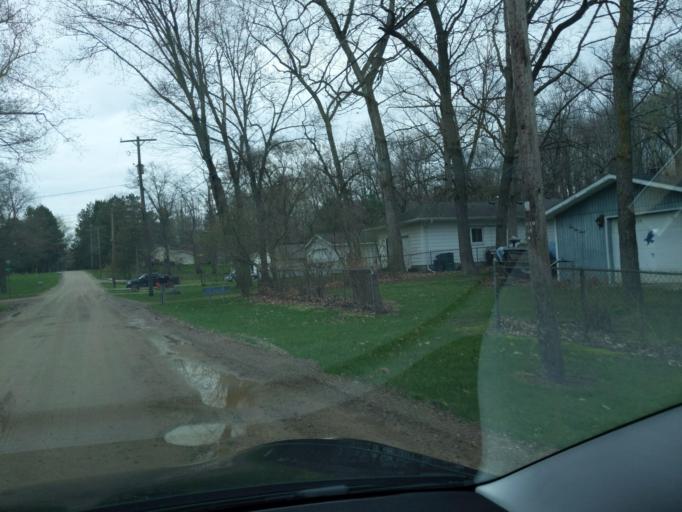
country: US
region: Michigan
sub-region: Ingham County
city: Stockbridge
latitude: 42.4395
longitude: -84.1012
